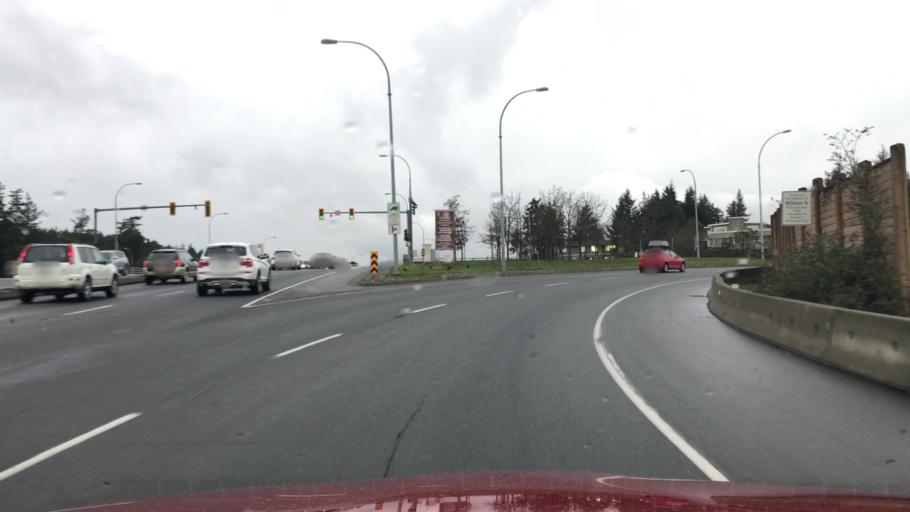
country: CA
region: British Columbia
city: Langford
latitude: 48.4558
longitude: -123.4965
